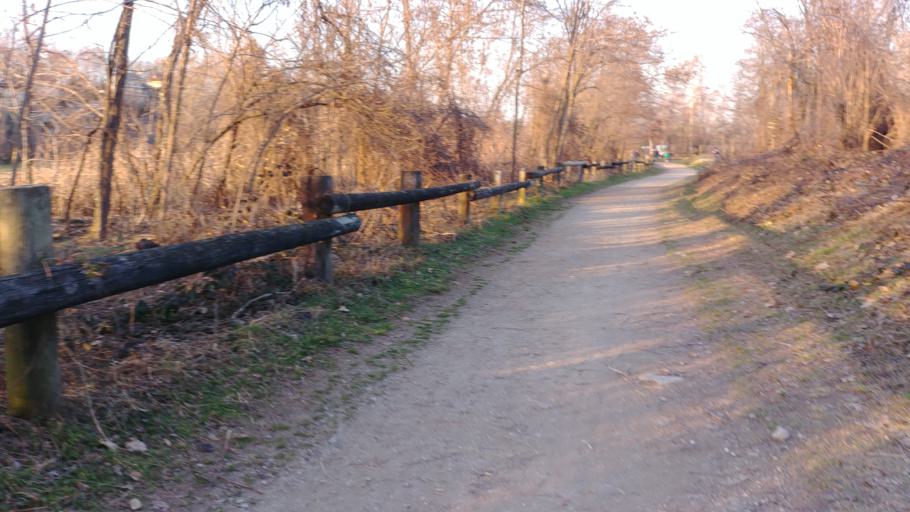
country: IT
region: Piedmont
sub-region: Provincia di Cuneo
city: Cuneo
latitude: 44.3645
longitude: 7.5391
